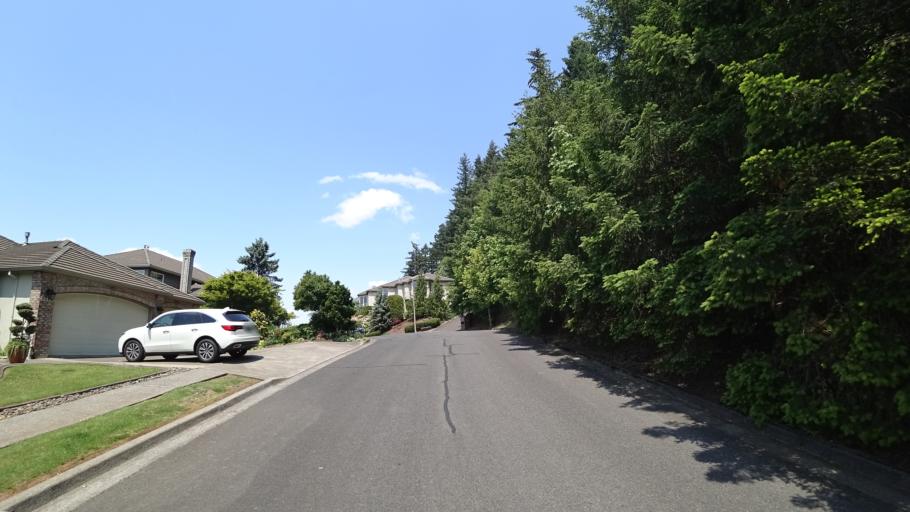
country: US
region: Oregon
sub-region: Clackamas County
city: Happy Valley
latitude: 45.4523
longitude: -122.5573
